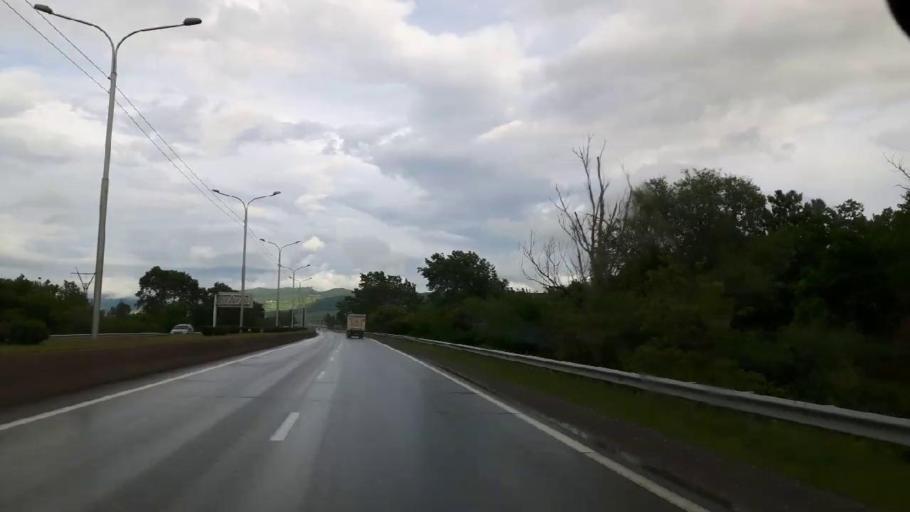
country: GE
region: Shida Kartli
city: Kaspi
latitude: 41.9108
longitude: 44.5668
